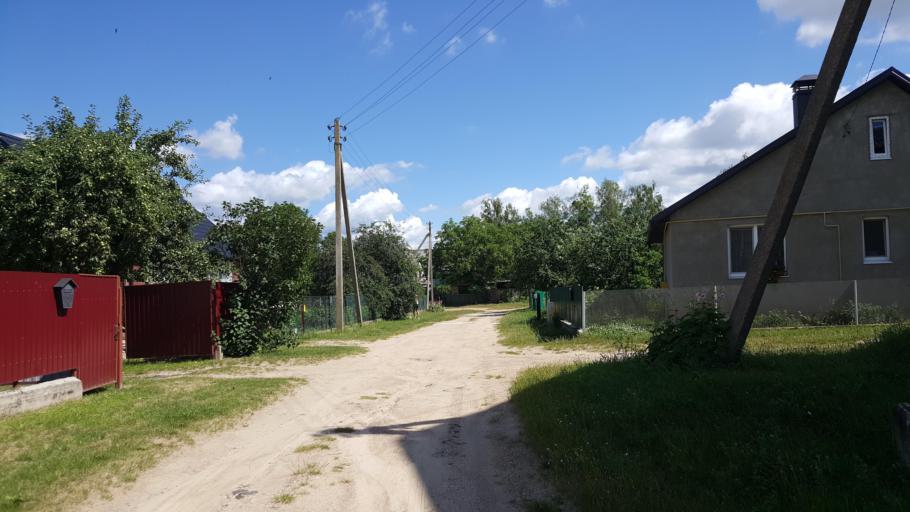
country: BY
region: Brest
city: Kamyanyets
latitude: 52.3915
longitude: 23.8296
